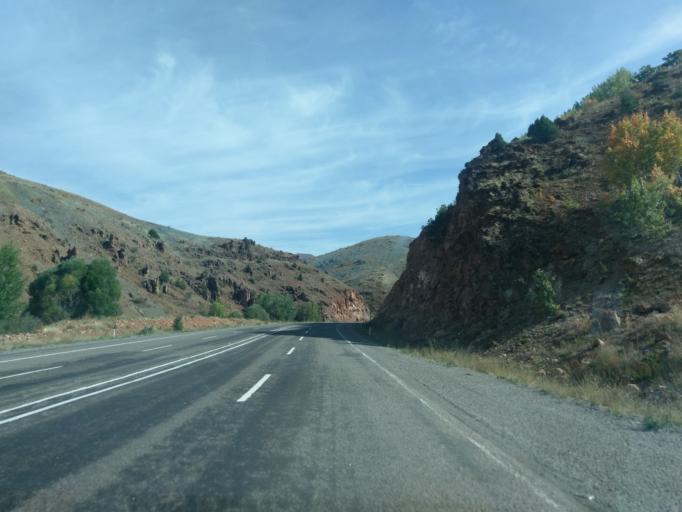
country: TR
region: Sivas
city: Imranli
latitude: 39.8582
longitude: 38.3161
